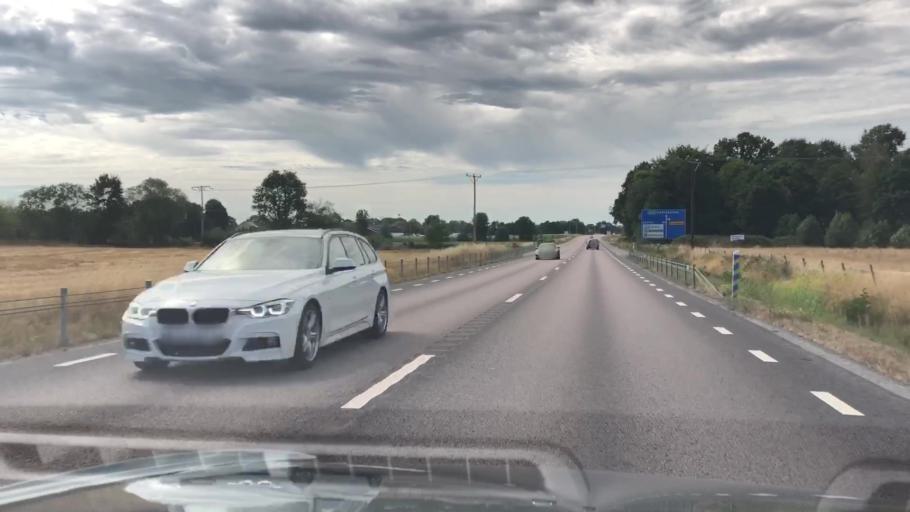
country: SE
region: Kalmar
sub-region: Torsas Kommun
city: Torsas
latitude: 56.3275
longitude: 16.0395
